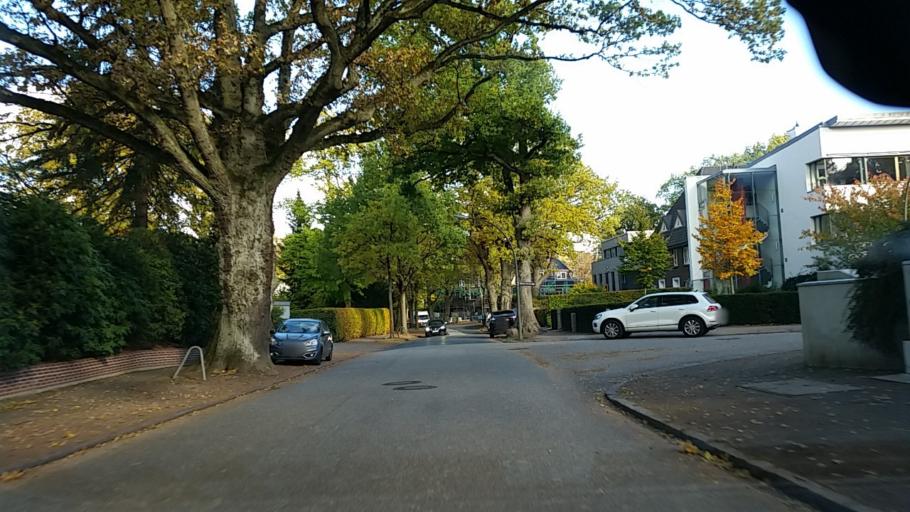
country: DE
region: Hamburg
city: Eidelstedt
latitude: 53.5610
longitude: 9.8671
